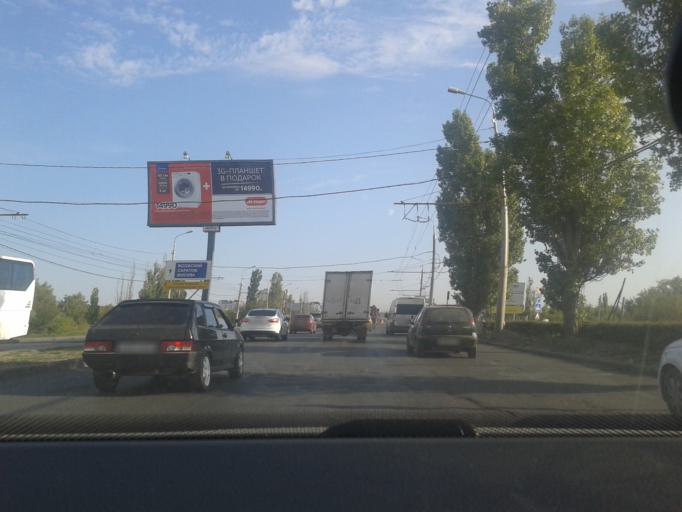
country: RU
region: Volgograd
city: Volgograd
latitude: 48.6324
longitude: 44.4288
